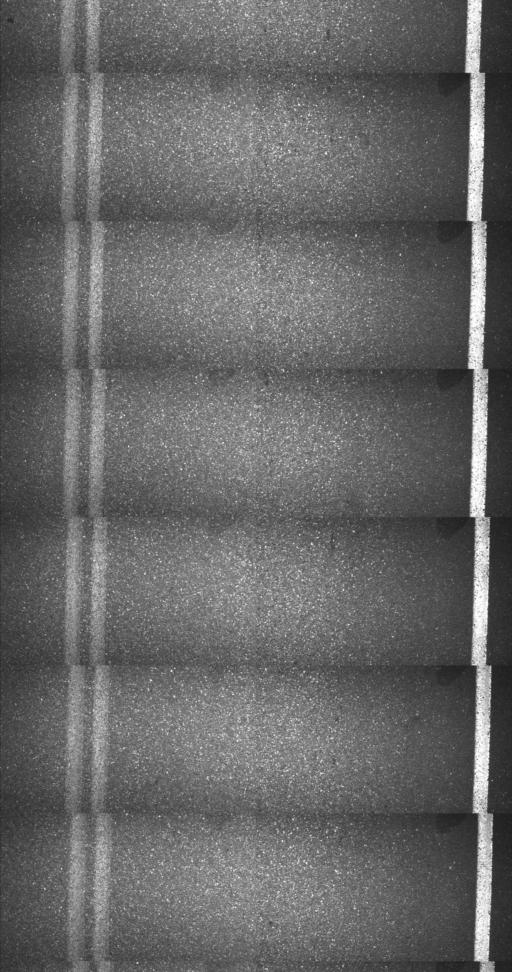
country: US
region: Vermont
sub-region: Orleans County
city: Newport
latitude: 44.8865
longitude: -71.9620
